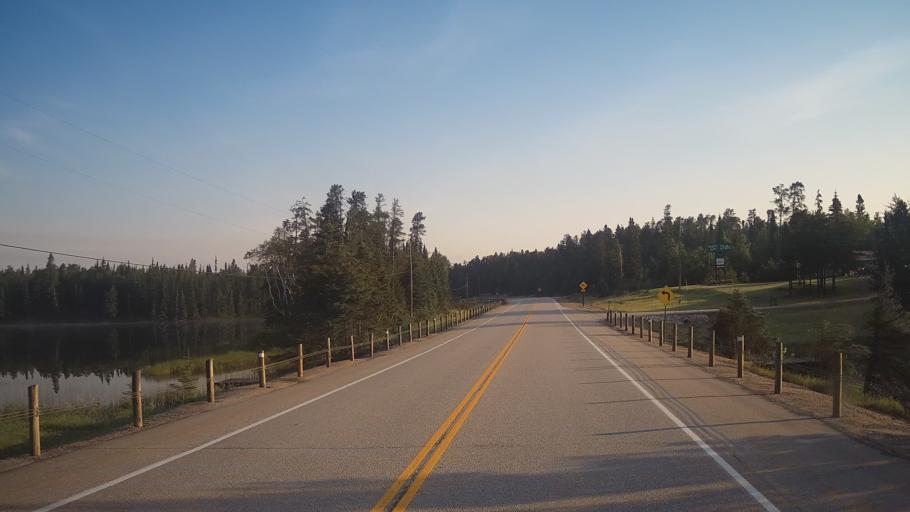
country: CA
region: Ontario
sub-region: Rainy River District
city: Atikokan
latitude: 49.2284
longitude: -90.9654
